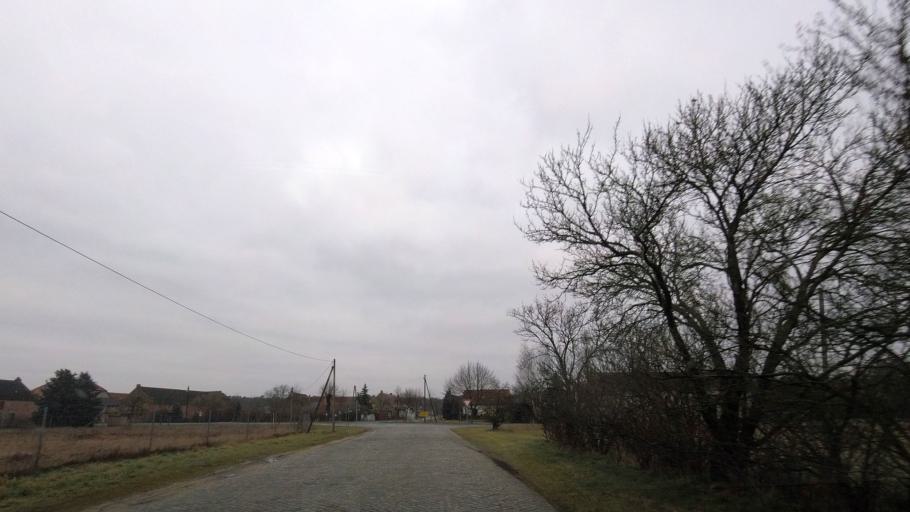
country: DE
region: Brandenburg
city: Beelitz
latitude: 52.1381
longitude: 12.9896
